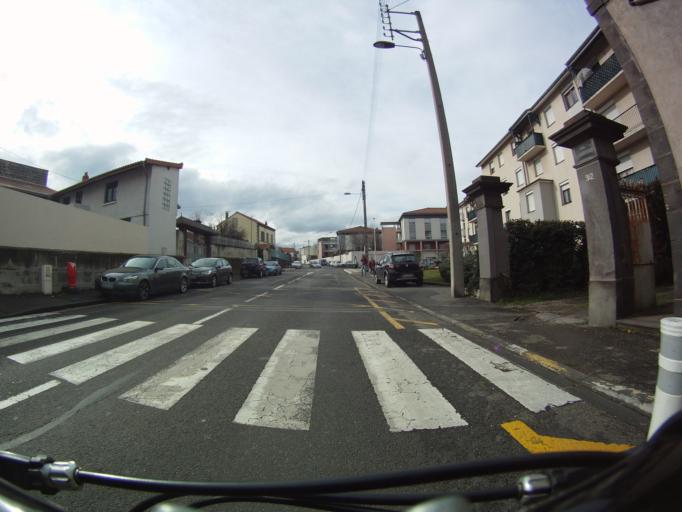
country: FR
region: Auvergne
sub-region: Departement du Puy-de-Dome
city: Aubiere
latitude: 45.7488
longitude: 3.1111
